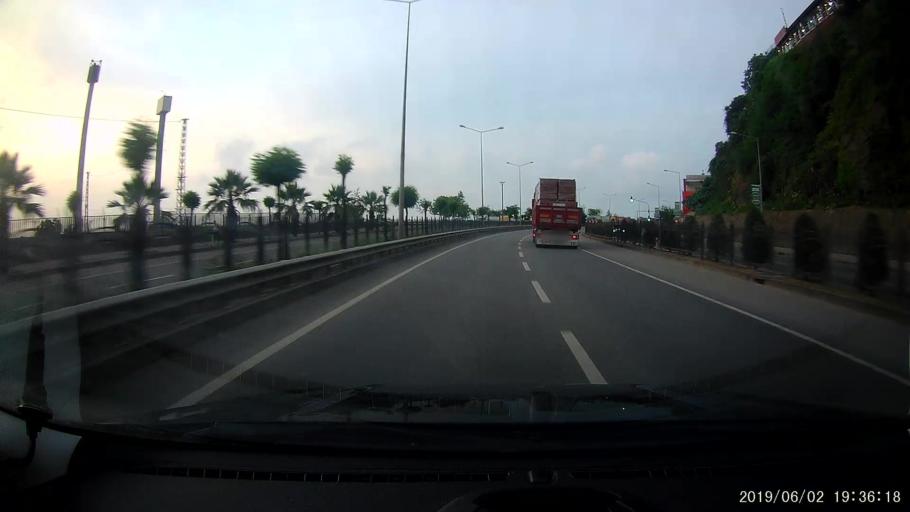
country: TR
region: Giresun
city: Giresun
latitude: 40.9222
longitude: 38.3867
